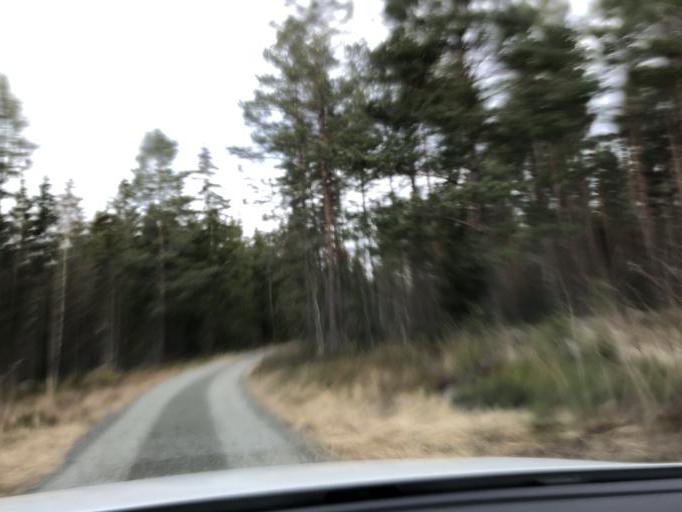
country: SE
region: Uppsala
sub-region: Heby Kommun
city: OEstervala
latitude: 60.3272
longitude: 17.1743
